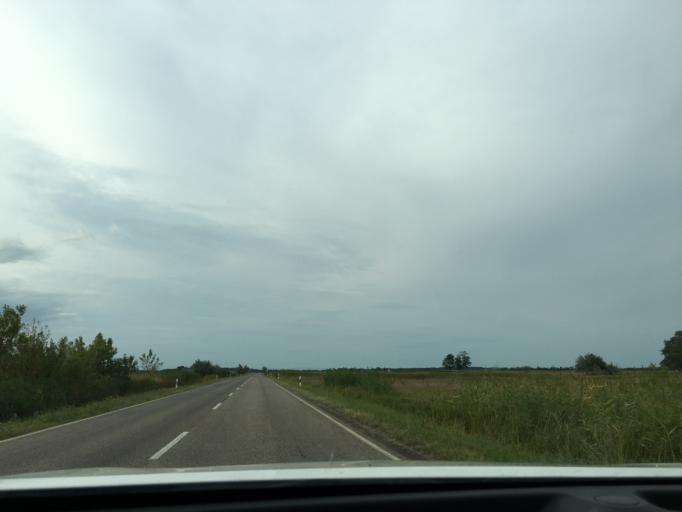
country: HU
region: Hajdu-Bihar
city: Egyek
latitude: 47.5706
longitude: 20.8600
